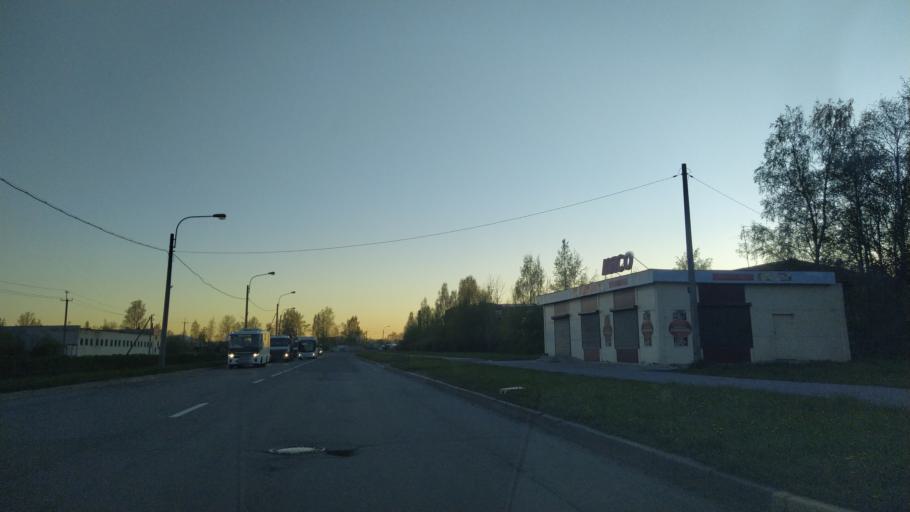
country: RU
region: St.-Petersburg
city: Pushkin
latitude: 59.7006
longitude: 30.3857
